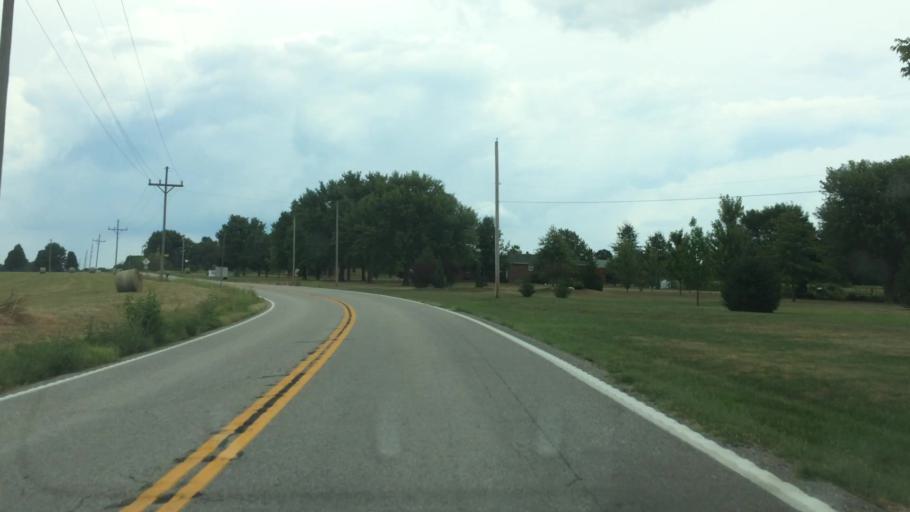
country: US
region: Missouri
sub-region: Greene County
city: Strafford
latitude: 37.2440
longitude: -93.1357
